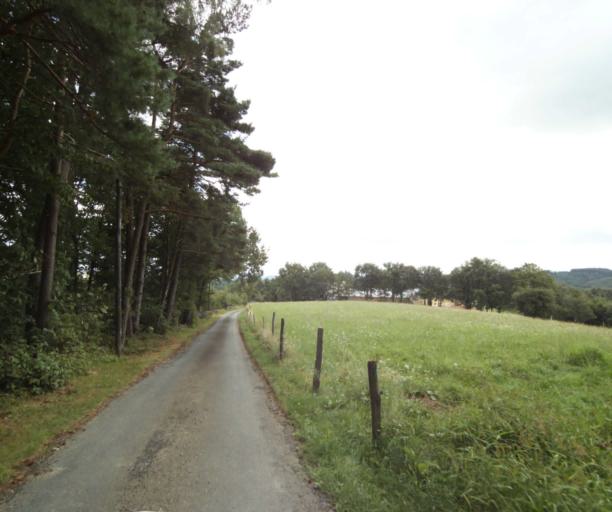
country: FR
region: Limousin
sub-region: Departement de la Correze
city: Sainte-Fortunade
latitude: 45.1965
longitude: 1.8460
